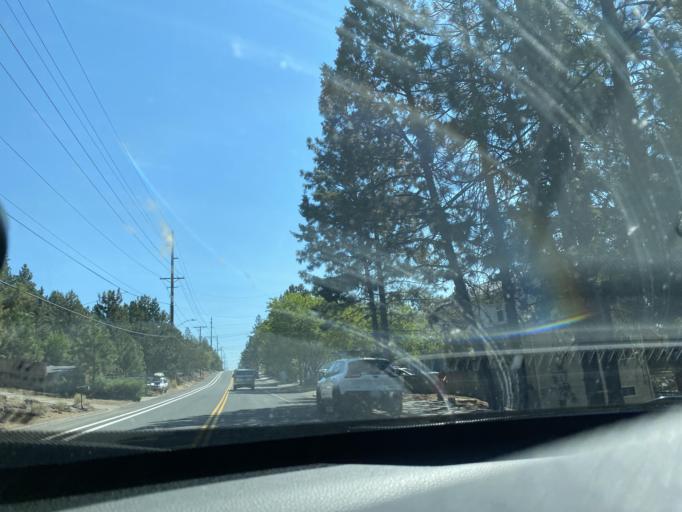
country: US
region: Oregon
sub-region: Deschutes County
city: Bend
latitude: 44.0642
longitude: -121.3373
